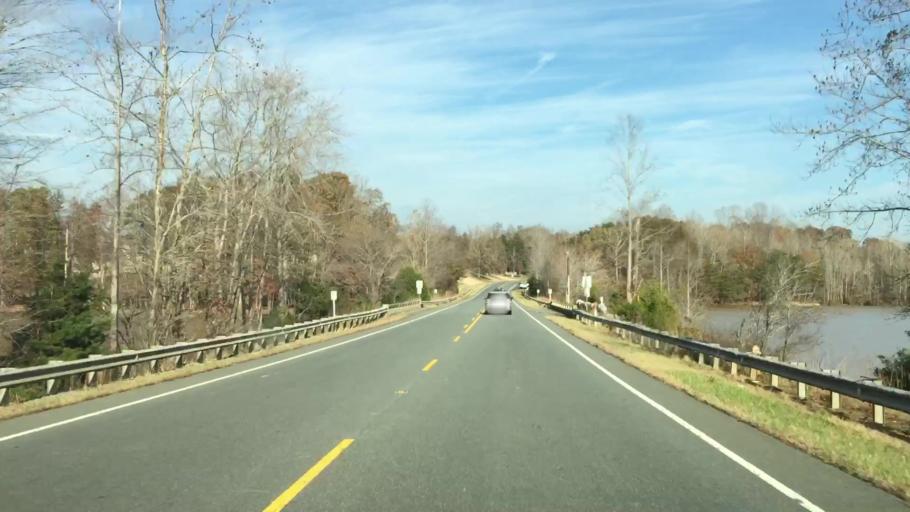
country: US
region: North Carolina
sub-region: Guilford County
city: Stokesdale
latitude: 36.2255
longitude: -80.0449
